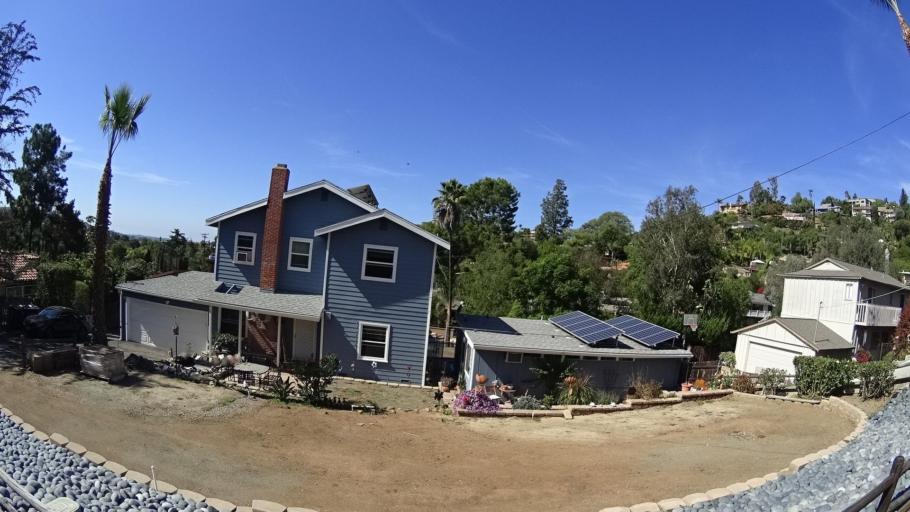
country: US
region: California
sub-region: San Diego County
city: Casa de Oro-Mount Helix
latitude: 32.7573
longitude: -116.9659
